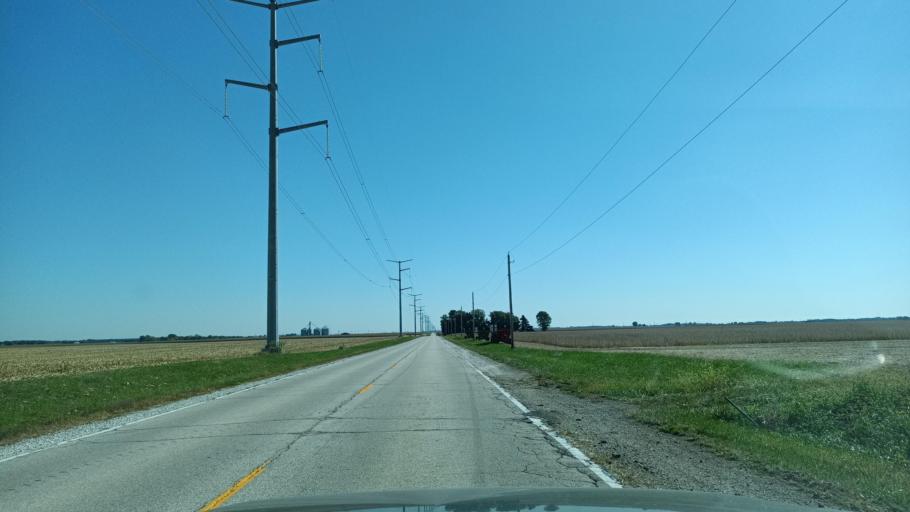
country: US
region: Illinois
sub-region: Peoria County
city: Elmwood
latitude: 40.9024
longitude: -90.0383
